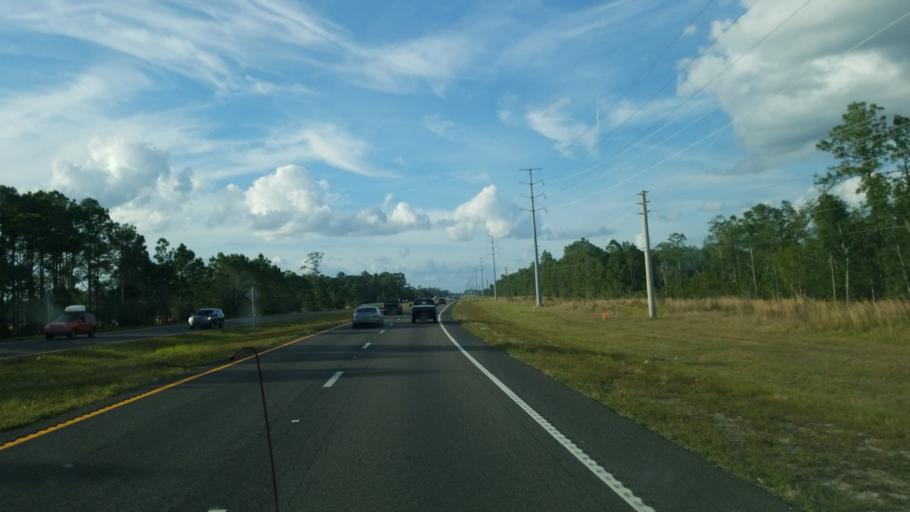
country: US
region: Florida
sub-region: Osceola County
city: Saint Cloud
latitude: 28.1989
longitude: -81.1658
